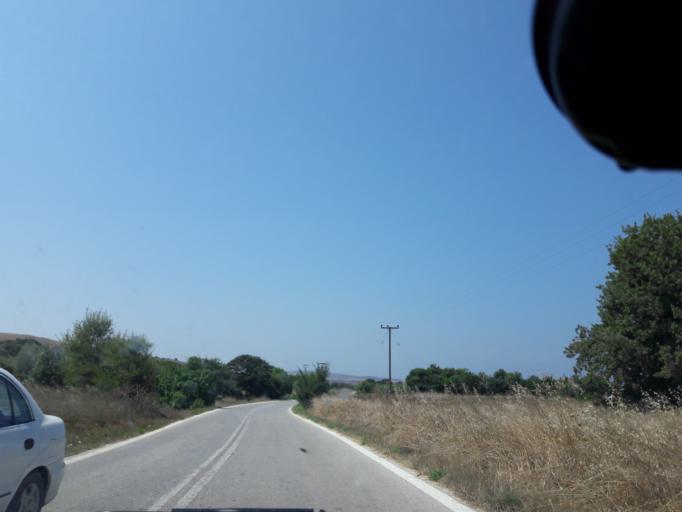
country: GR
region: North Aegean
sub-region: Nomos Lesvou
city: Myrina
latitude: 39.9272
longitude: 25.2973
